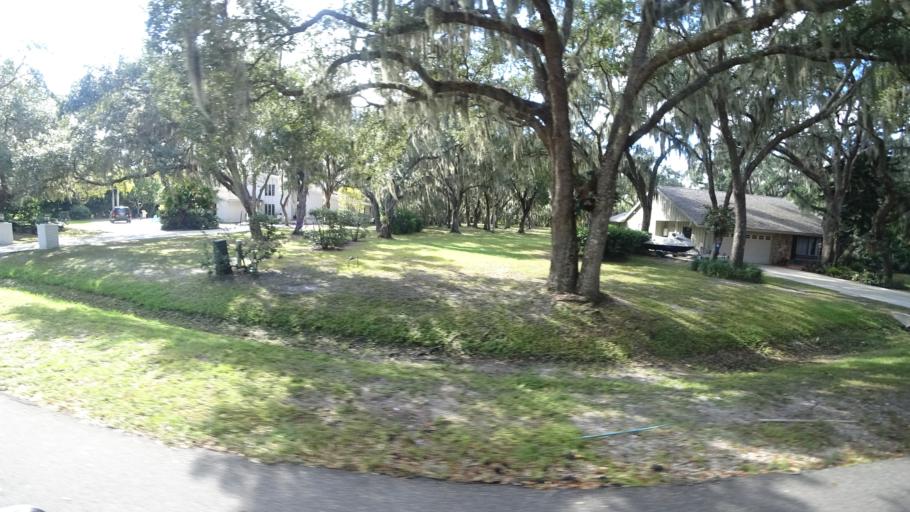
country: US
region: Florida
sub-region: Sarasota County
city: North Sarasota
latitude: 27.3972
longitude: -82.5222
